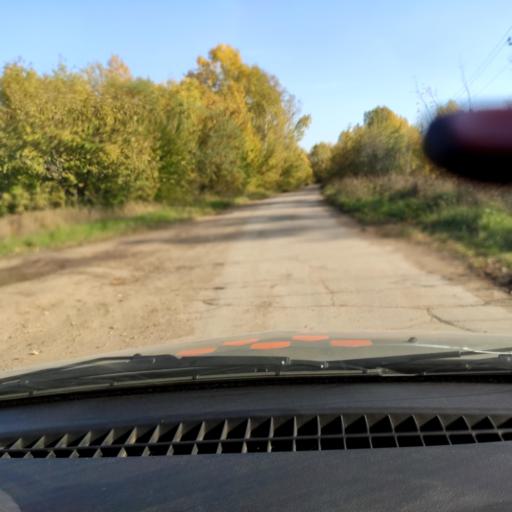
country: RU
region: Bashkortostan
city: Iglino
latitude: 54.7968
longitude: 56.2242
